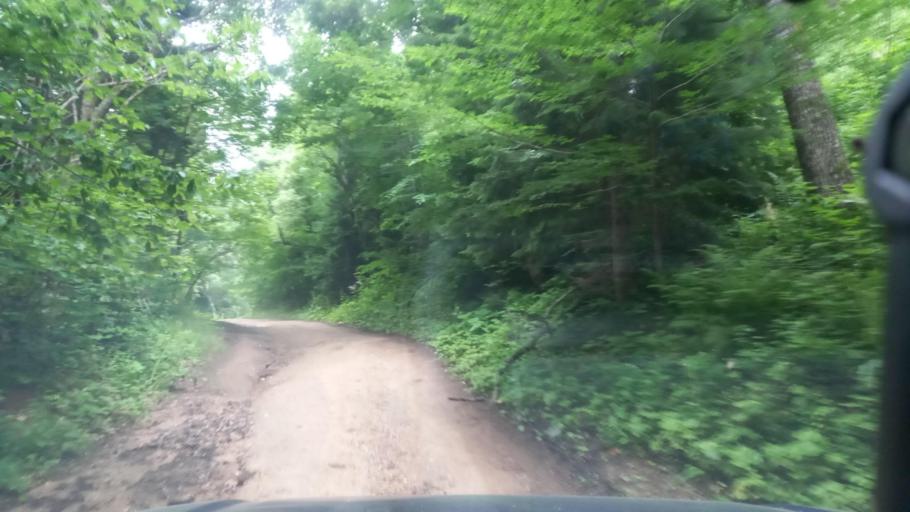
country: RU
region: Karachayevo-Cherkesiya
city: Kurdzhinovo
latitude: 43.8071
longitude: 40.8586
